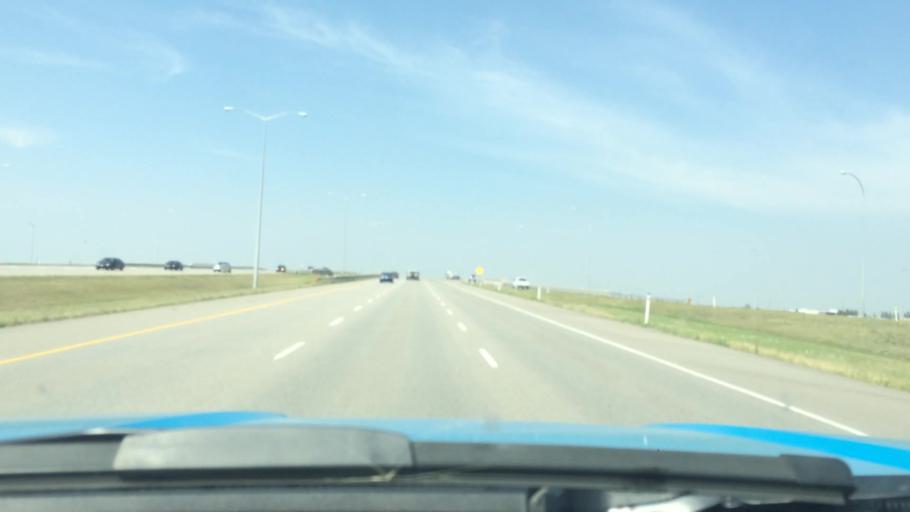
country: CA
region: Alberta
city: Chestermere
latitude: 50.9454
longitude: -113.9202
